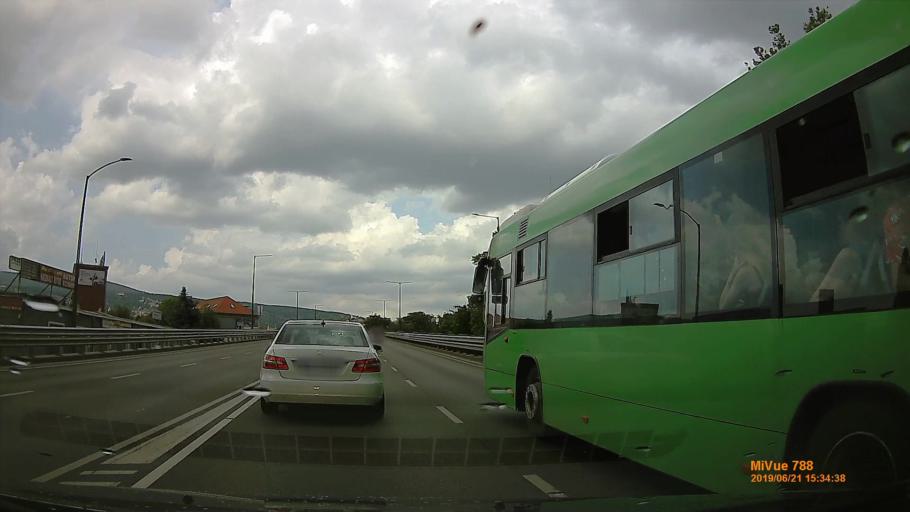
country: HU
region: Baranya
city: Pecs
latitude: 46.0654
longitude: 18.2315
